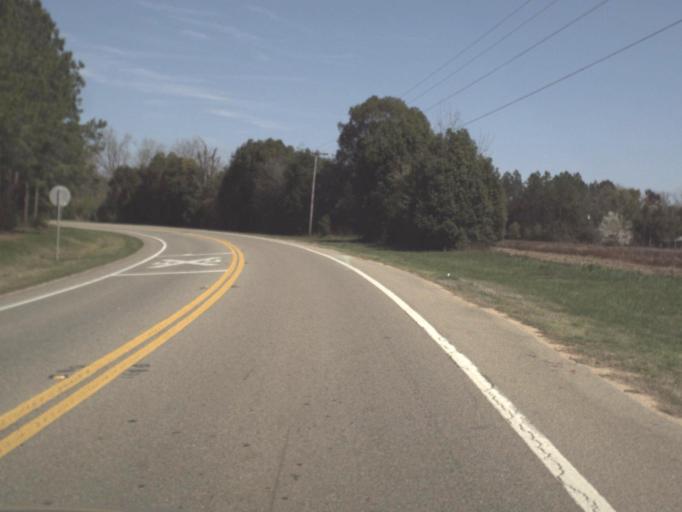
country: US
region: Florida
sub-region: Gadsden County
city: Gretna
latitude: 30.5640
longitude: -84.7457
